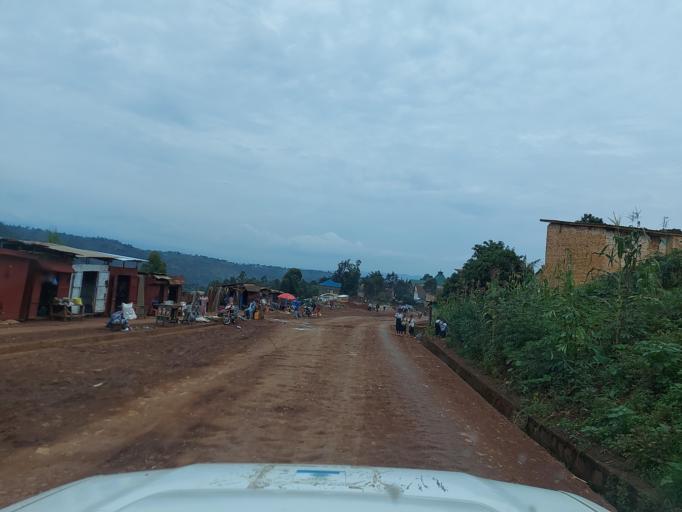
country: CD
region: South Kivu
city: Bukavu
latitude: -2.4781
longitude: 28.8225
